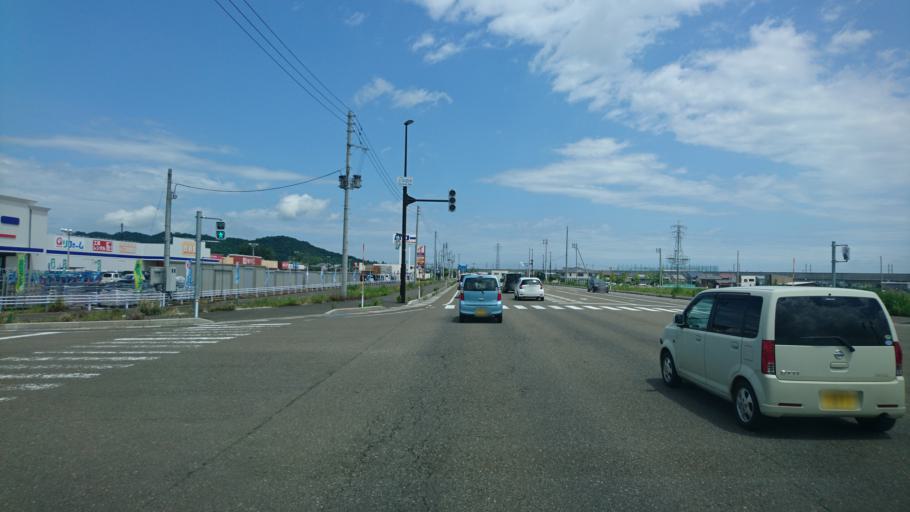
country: JP
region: Niigata
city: Joetsu
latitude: 37.0884
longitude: 138.2335
